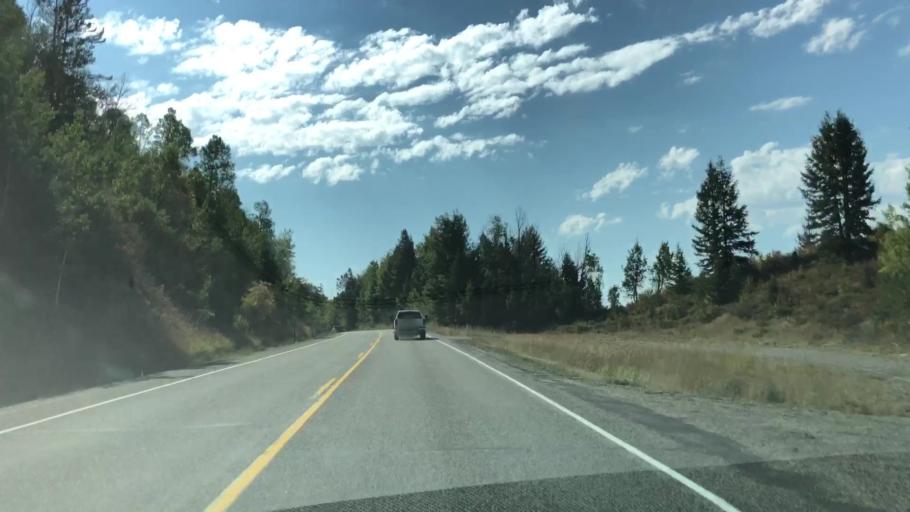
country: US
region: Idaho
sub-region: Teton County
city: Victor
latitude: 43.2821
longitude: -111.1189
